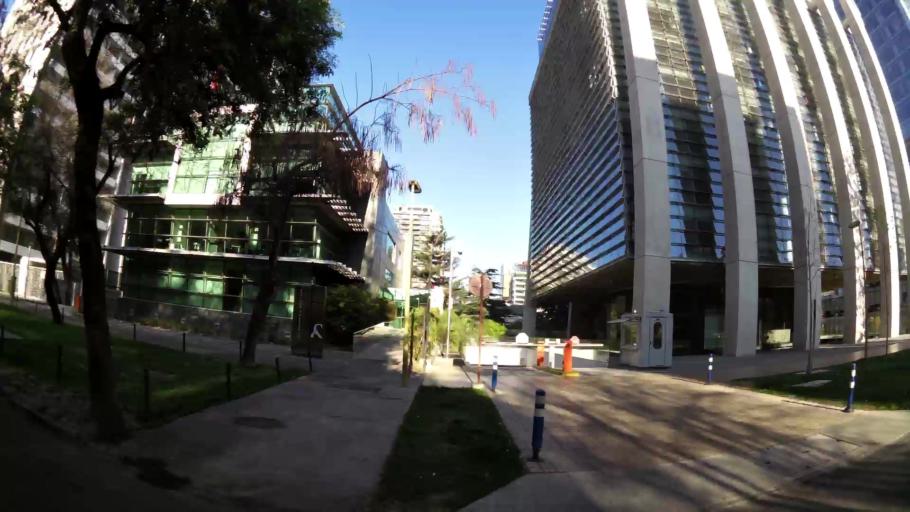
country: CL
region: Santiago Metropolitan
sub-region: Provincia de Santiago
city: Villa Presidente Frei, Nunoa, Santiago, Chile
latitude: -33.4165
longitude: -70.5895
